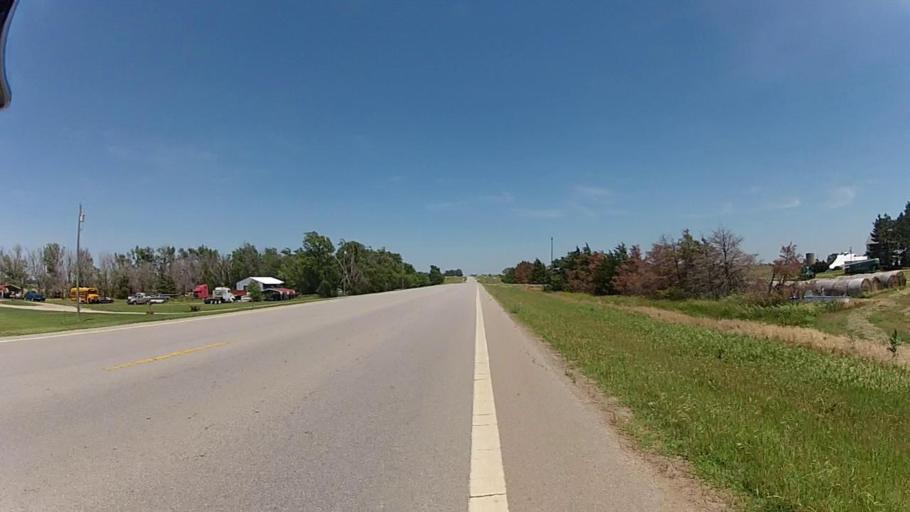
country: US
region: Kansas
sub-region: Harper County
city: Harper
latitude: 37.2386
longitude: -98.1213
